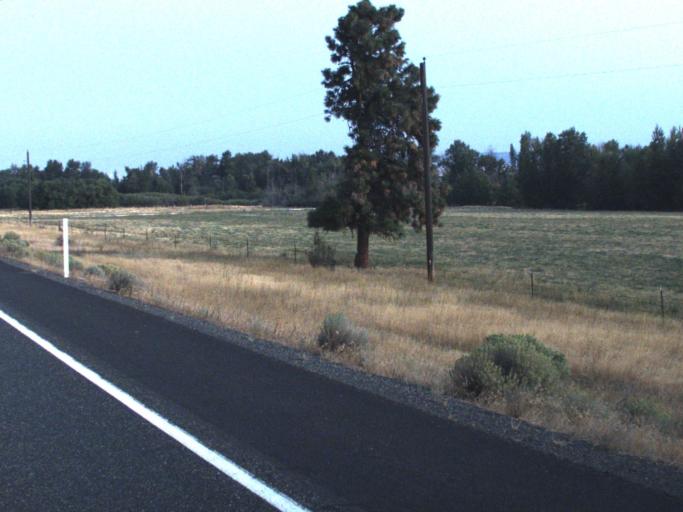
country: US
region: Washington
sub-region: Kittitas County
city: Ellensburg
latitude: 47.0796
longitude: -120.6371
